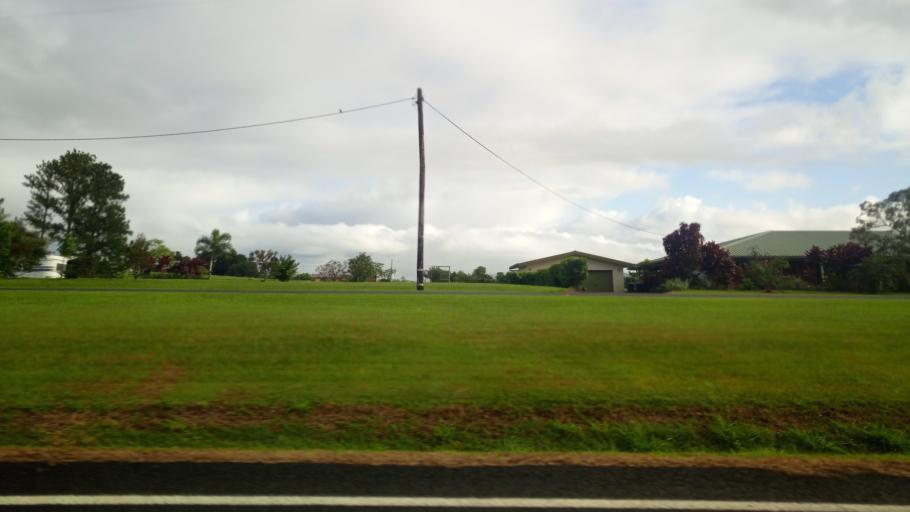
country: AU
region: Queensland
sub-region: Cassowary Coast
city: Innisfail
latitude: -17.5555
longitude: 145.9581
